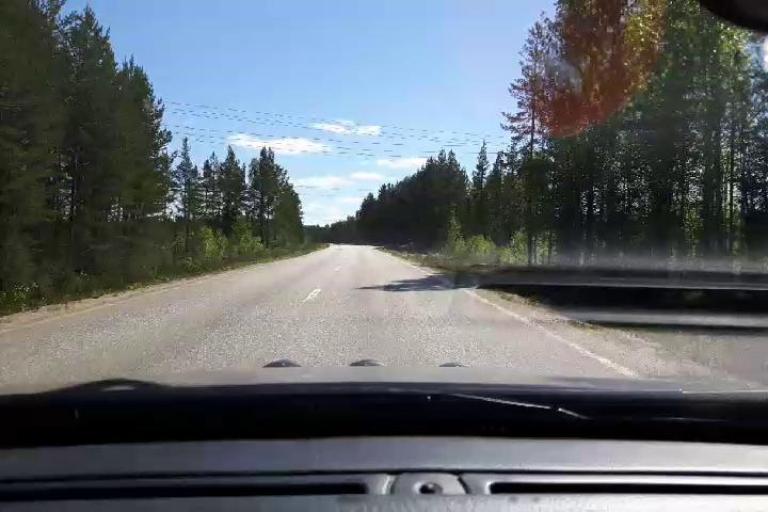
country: SE
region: Vaesternorrland
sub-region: Ange Kommun
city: Ange
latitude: 62.0676
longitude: 15.1062
